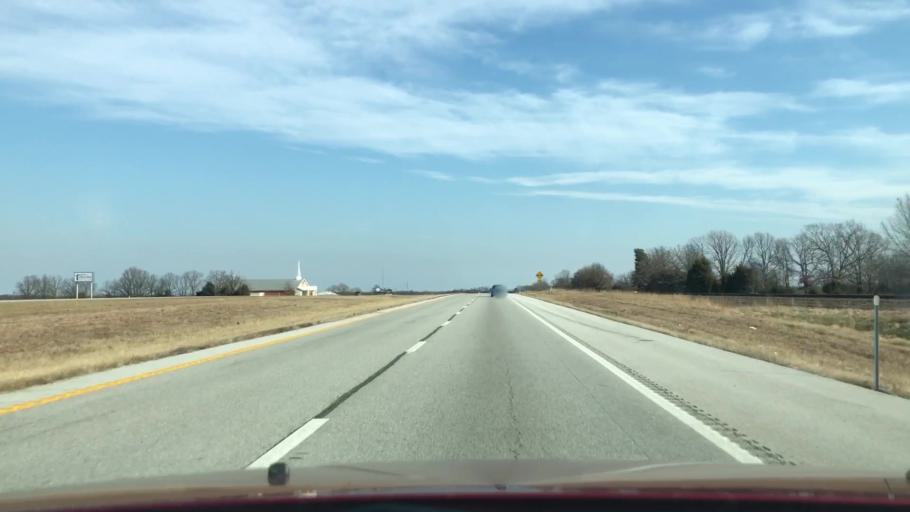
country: US
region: Missouri
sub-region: Webster County
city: Seymour
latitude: 37.1674
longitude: -92.8711
